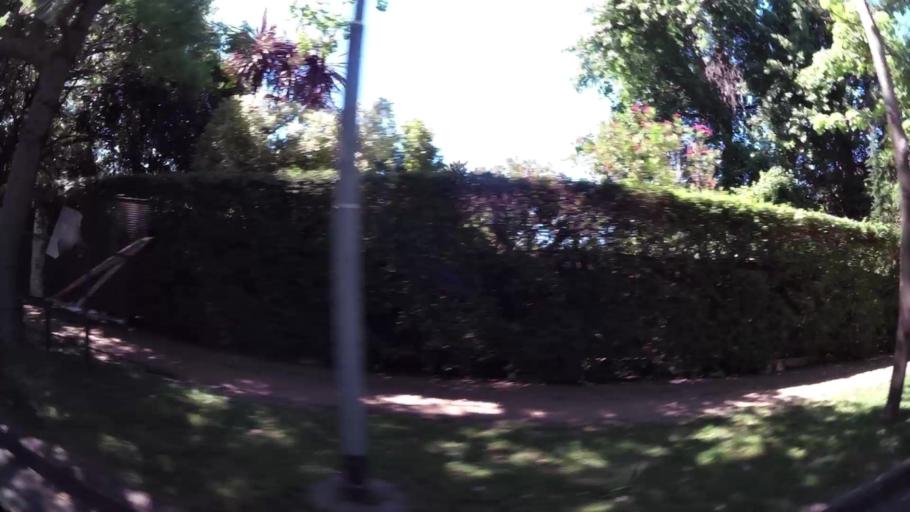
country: AR
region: Buenos Aires
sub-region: Partido de Tigre
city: Tigre
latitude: -34.4968
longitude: -58.6234
